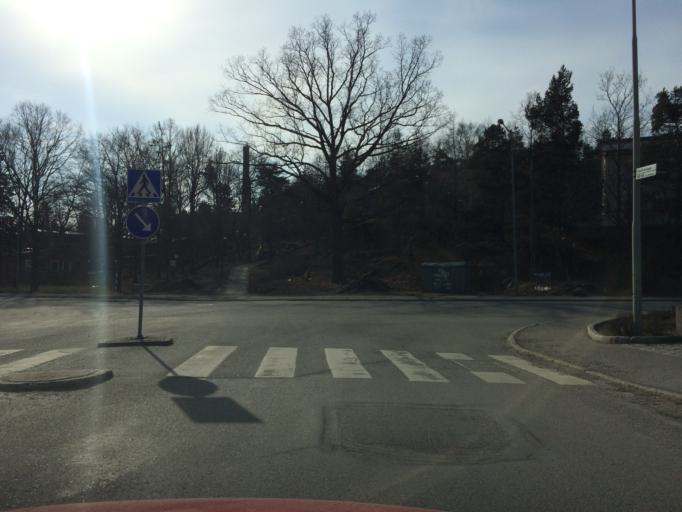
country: SE
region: Stockholm
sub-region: Stockholms Kommun
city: Arsta
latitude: 59.2919
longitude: 18.0051
